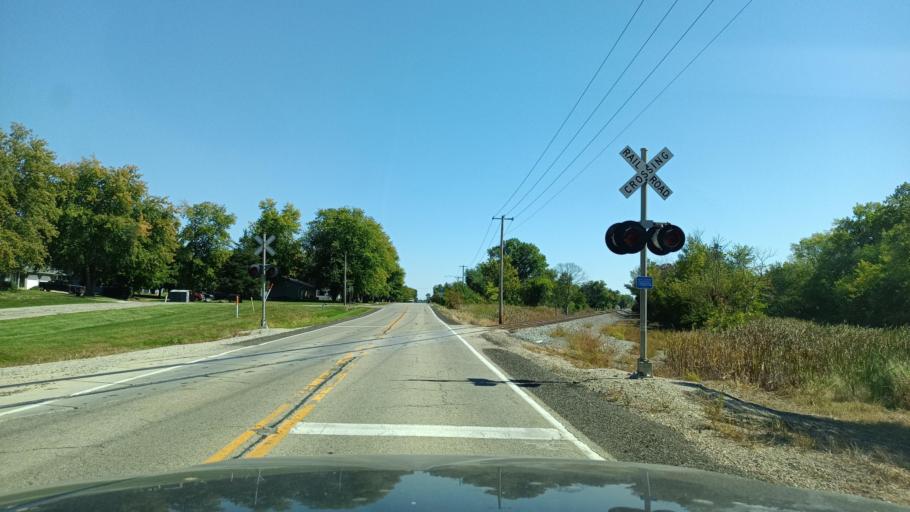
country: US
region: Illinois
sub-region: McLean County
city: Danvers
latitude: 40.6171
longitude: -89.2126
